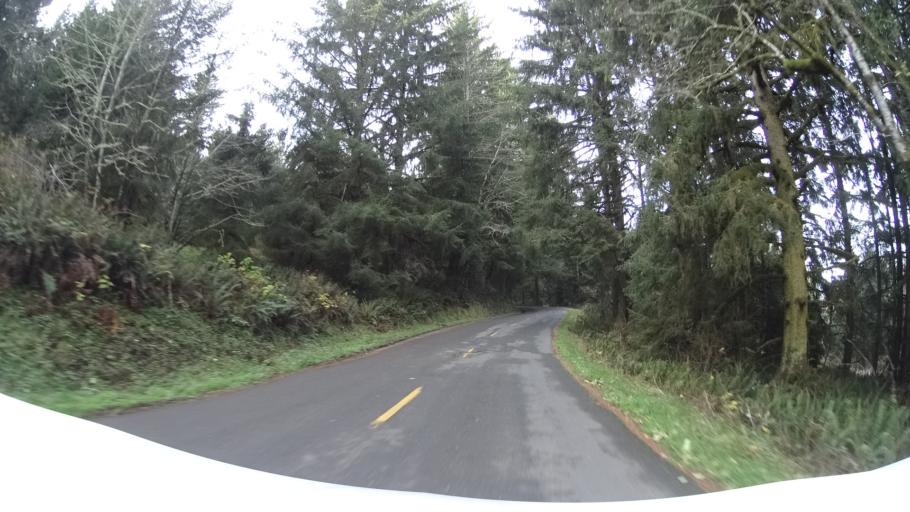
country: US
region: California
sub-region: Humboldt County
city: Ferndale
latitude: 40.5379
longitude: -124.2763
